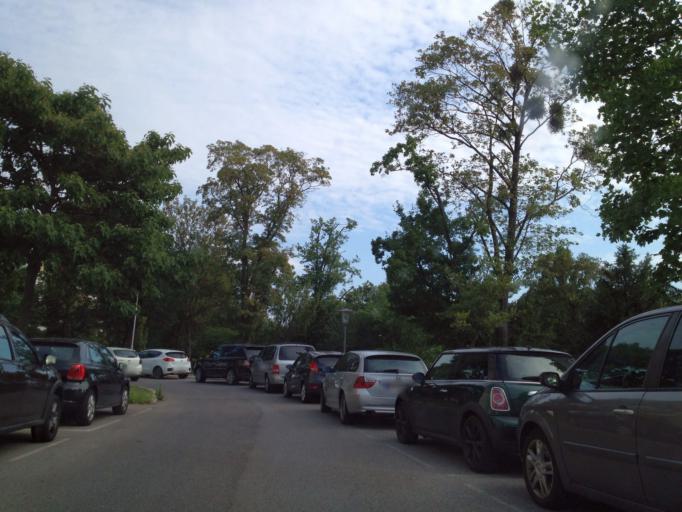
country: AT
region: Lower Austria
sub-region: Politischer Bezirk Modling
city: Perchtoldsdorf
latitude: 48.1699
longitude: 16.2777
